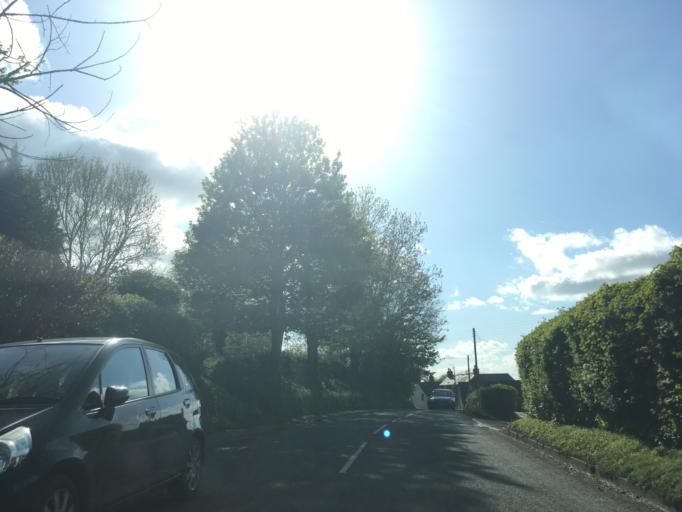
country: GB
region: England
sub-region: Gloucestershire
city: Stonehouse
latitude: 51.7290
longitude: -2.2532
